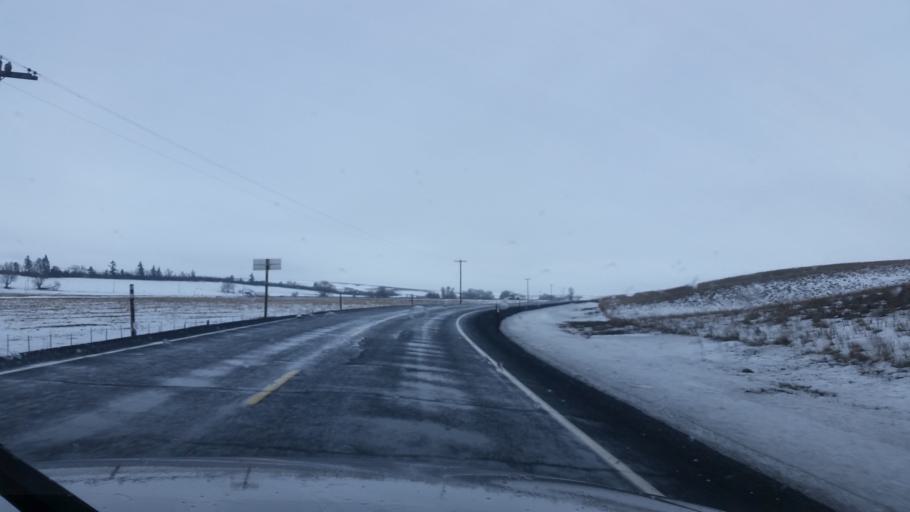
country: US
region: Washington
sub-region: Lincoln County
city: Davenport
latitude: 47.4632
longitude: -118.1840
